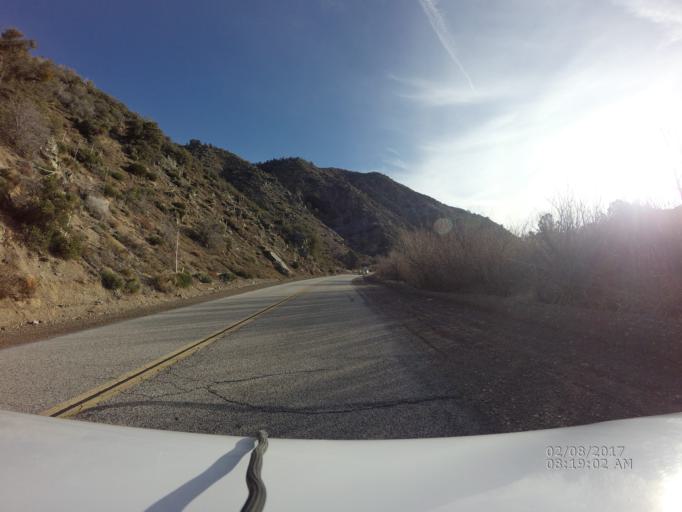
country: US
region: California
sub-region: San Bernardino County
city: Pinon Hills
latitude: 34.3975
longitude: -117.8072
